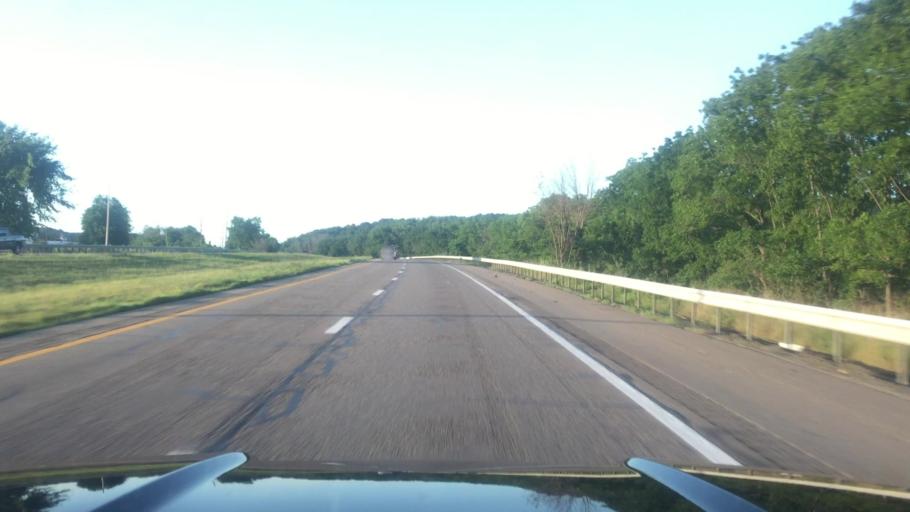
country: US
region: Ohio
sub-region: Tuscarawas County
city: New Philadelphia
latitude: 40.4515
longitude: -81.5049
